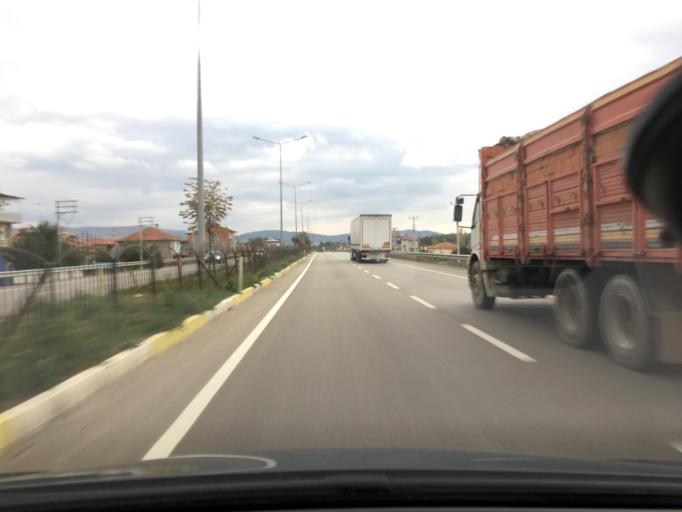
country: TR
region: Afyonkarahisar
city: Sincanli
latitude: 38.7752
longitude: 30.3713
